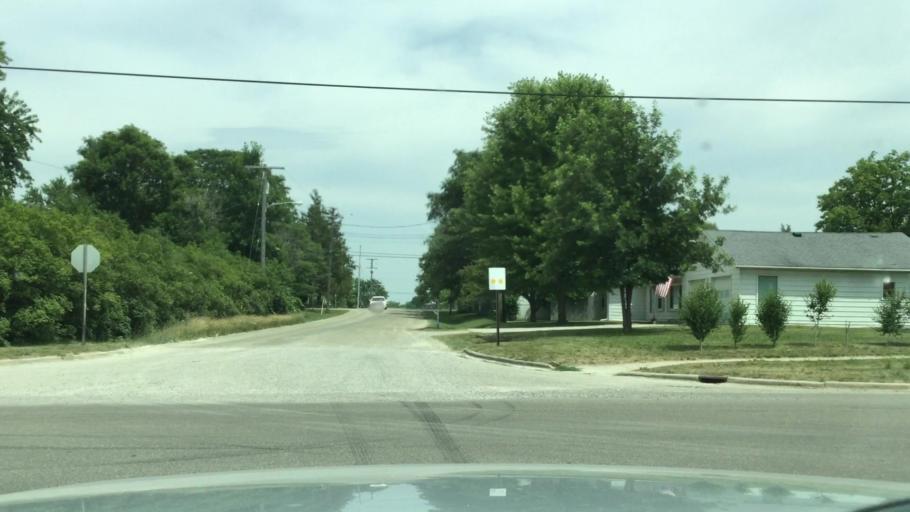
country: US
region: Michigan
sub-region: Genesee County
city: Flint
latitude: 42.9985
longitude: -83.7623
